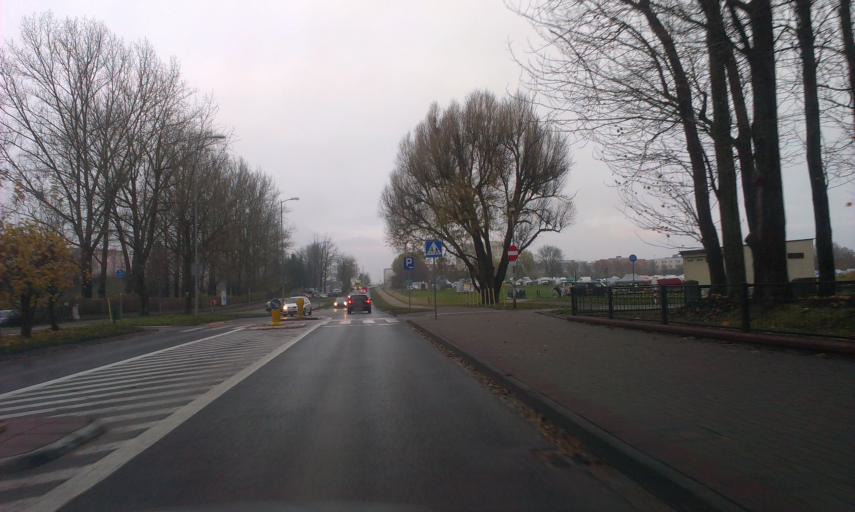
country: PL
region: West Pomeranian Voivodeship
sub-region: Koszalin
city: Koszalin
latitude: 54.1984
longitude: 16.2025
